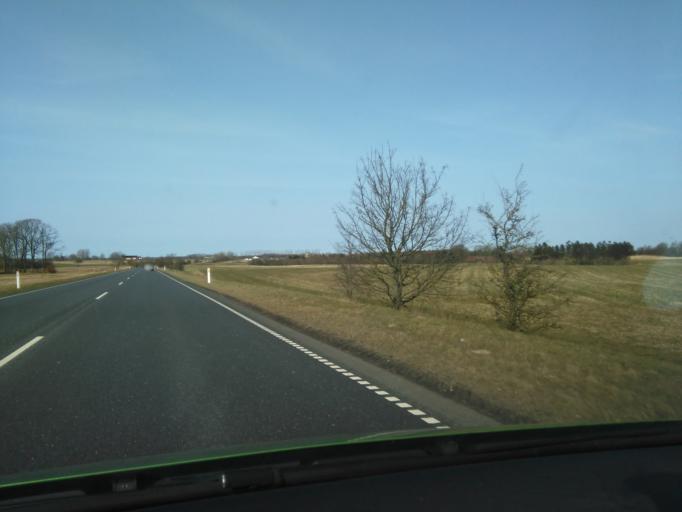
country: DK
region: Central Jutland
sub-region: Silkeborg Kommune
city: Kjellerup
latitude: 56.2670
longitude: 9.4255
